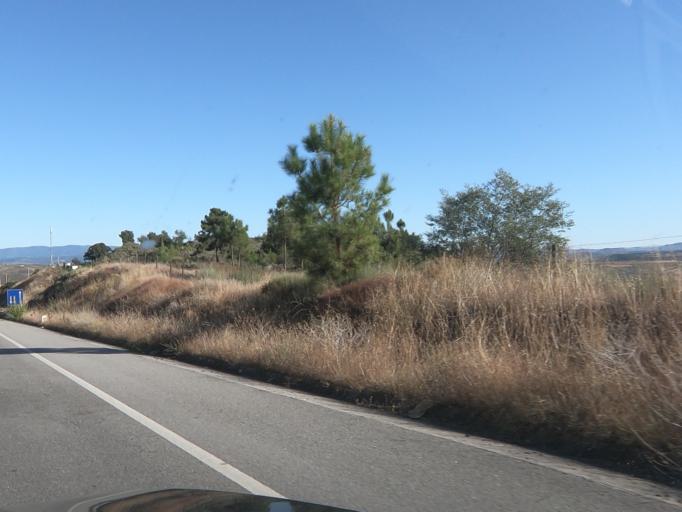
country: PT
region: Vila Real
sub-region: Valpacos
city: Valpacos
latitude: 41.5679
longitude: -7.2798
